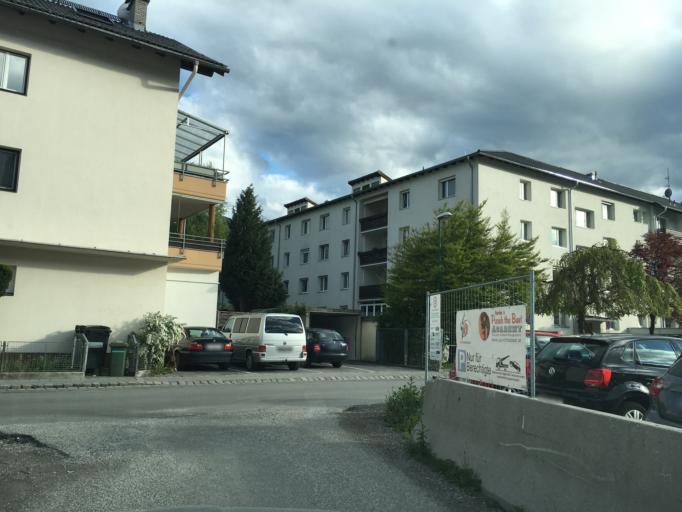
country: AT
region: Tyrol
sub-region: Politischer Bezirk Innsbruck Land
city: Rum
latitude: 47.2771
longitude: 11.4493
